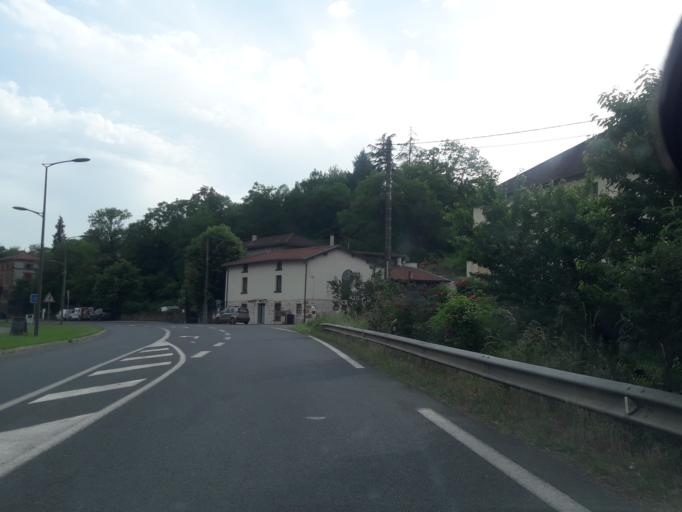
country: FR
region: Rhone-Alpes
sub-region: Departement du Rhone
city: Sain-Bel
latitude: 45.8183
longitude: 4.6048
